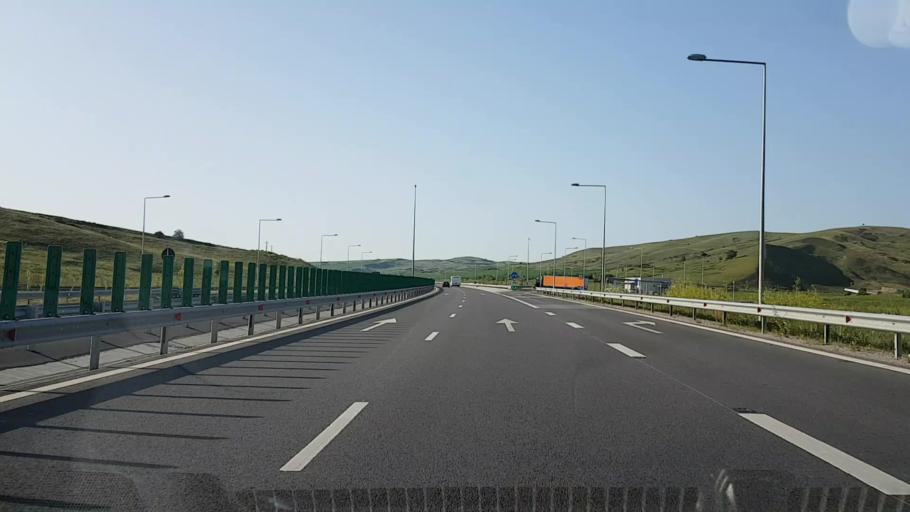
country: RO
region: Alba
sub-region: Comuna Unirea
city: Unirea
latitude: 46.4406
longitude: 23.7988
